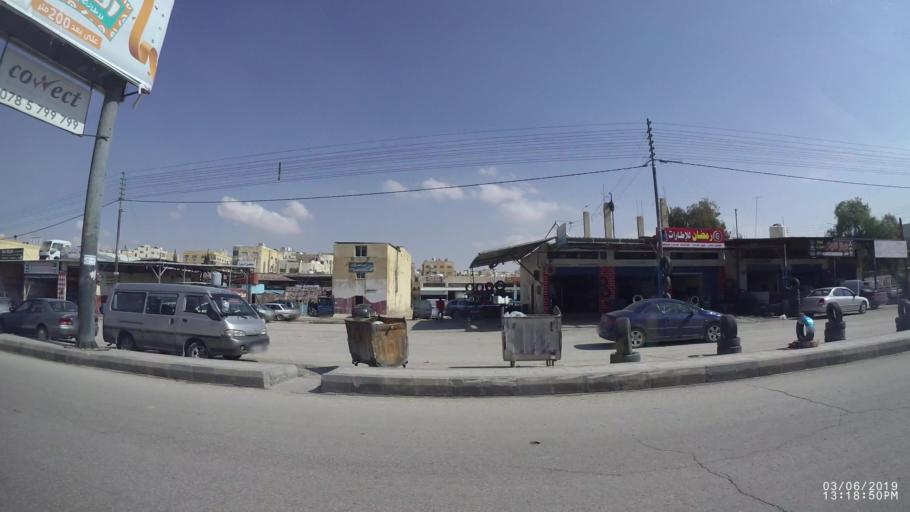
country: JO
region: Zarqa
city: Zarqa
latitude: 32.0389
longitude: 36.0932
